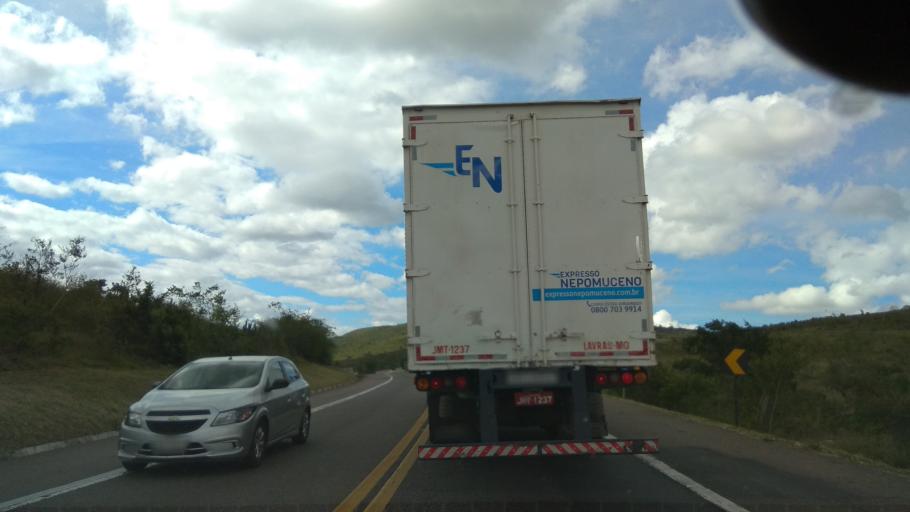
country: BR
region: Bahia
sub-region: Amargosa
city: Amargosa
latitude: -12.9122
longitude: -39.8657
